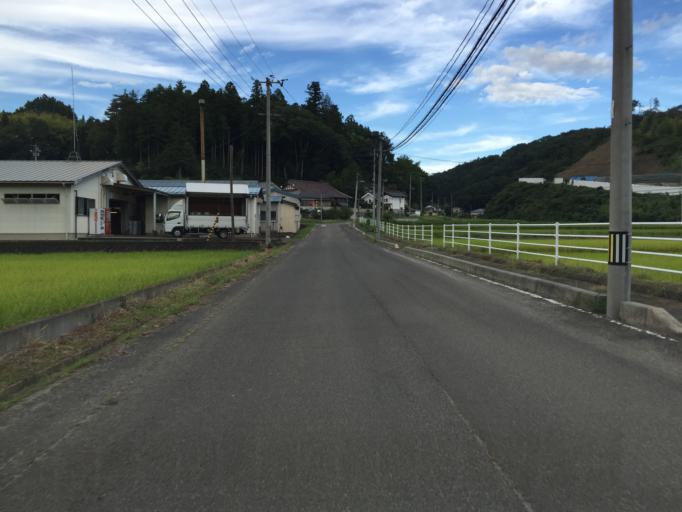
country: JP
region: Fukushima
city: Fukushima-shi
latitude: 37.6756
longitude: 140.5823
